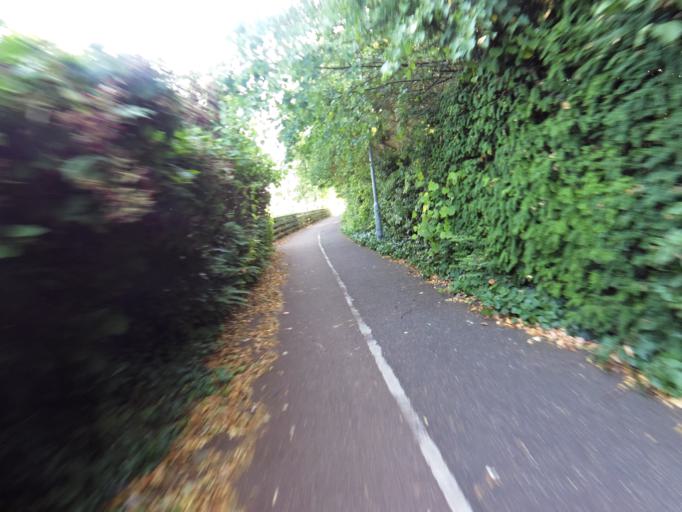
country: GB
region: England
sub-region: Essex
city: Chelmsford
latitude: 51.7499
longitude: 0.5116
